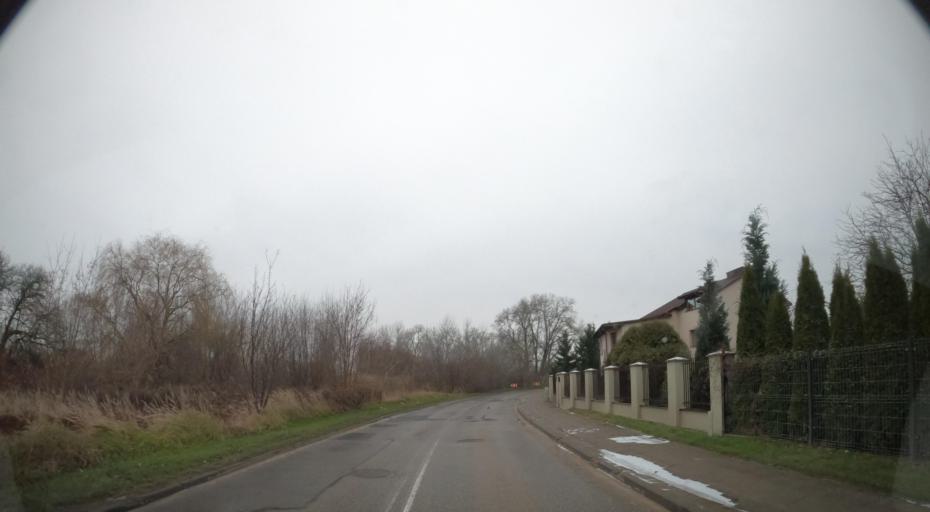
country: PL
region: Masovian Voivodeship
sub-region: Radom
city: Radom
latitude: 51.3804
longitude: 21.1917
